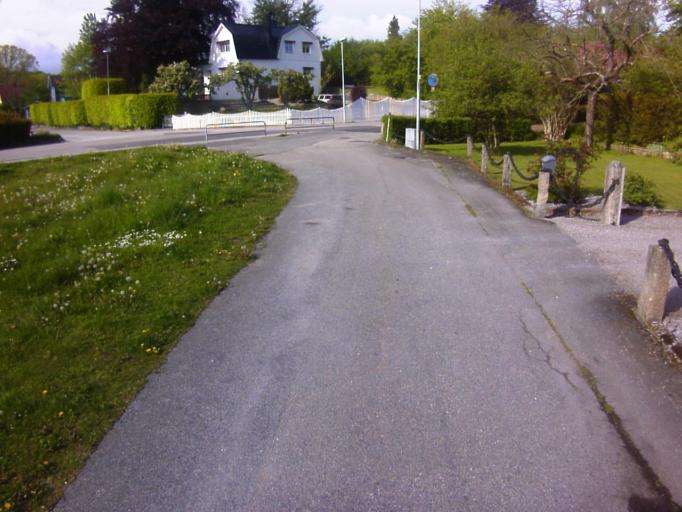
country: SE
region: Blekinge
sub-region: Solvesborgs Kommun
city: Soelvesborg
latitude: 56.0585
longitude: 14.5986
